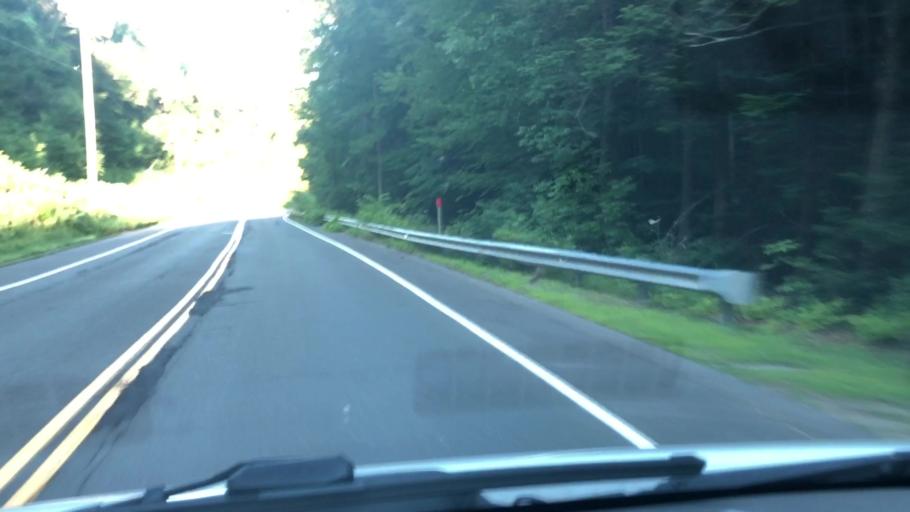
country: US
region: Massachusetts
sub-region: Hampshire County
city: Westhampton
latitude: 42.2840
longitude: -72.8463
